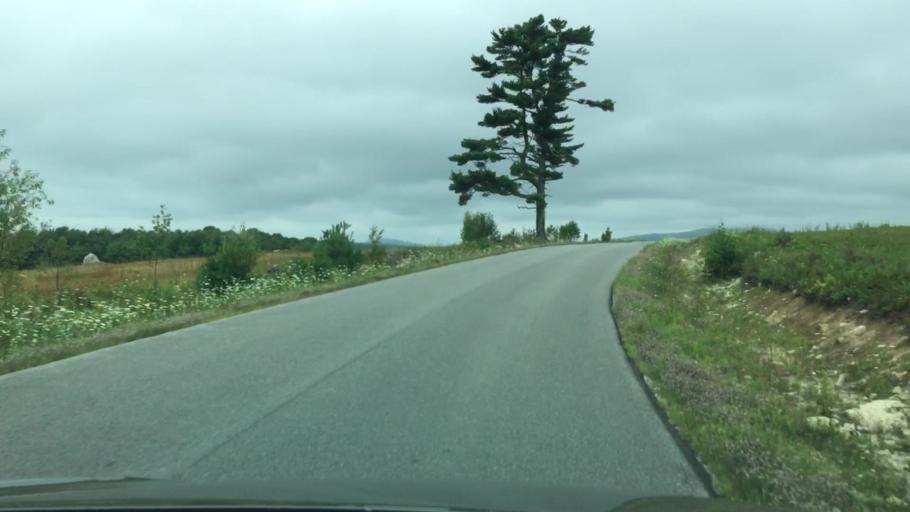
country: US
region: Maine
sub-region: Waldo County
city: Stockton Springs
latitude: 44.5218
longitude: -68.8809
